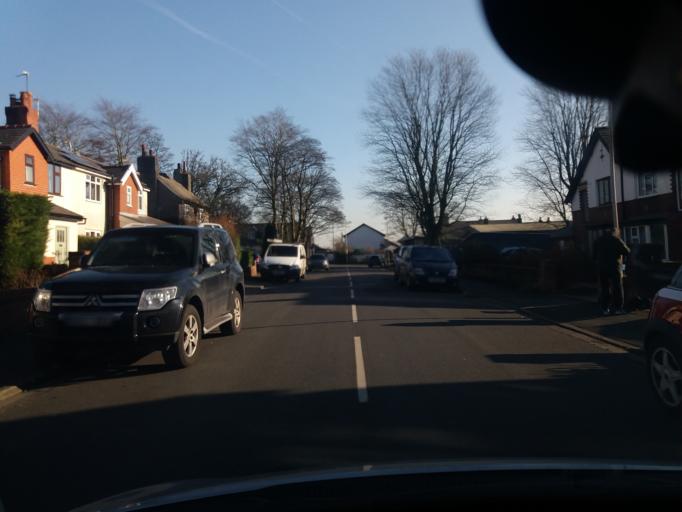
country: GB
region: England
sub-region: Lancashire
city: Adlington
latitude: 53.6157
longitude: -2.6019
